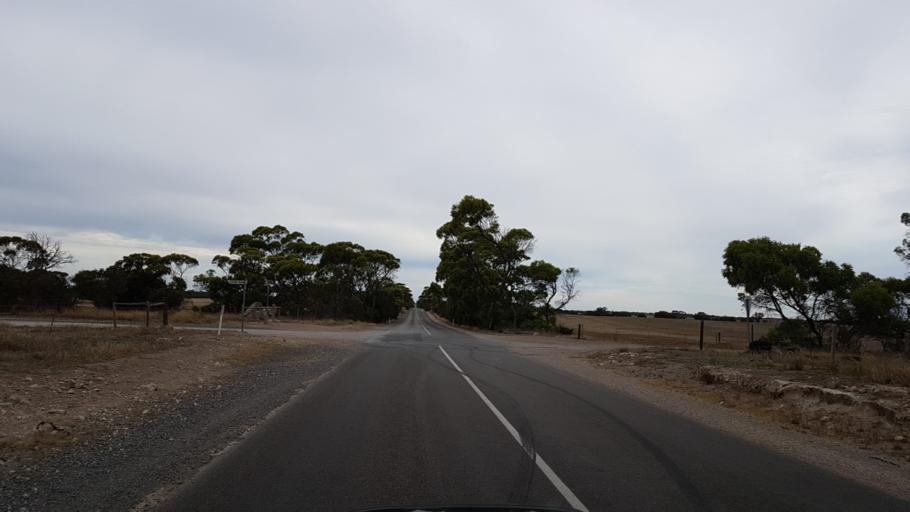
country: AU
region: South Australia
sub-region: Yorke Peninsula
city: Honiton
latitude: -34.9850
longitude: 137.2148
